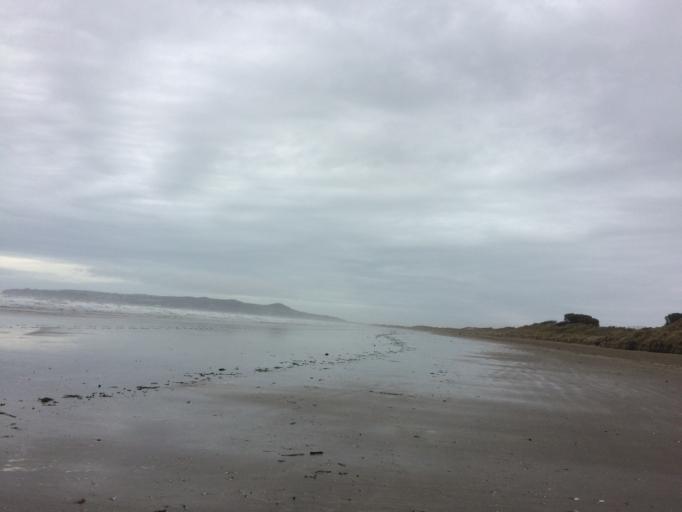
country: IE
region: Leinster
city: Portmarnock
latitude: 53.4278
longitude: -6.1232
